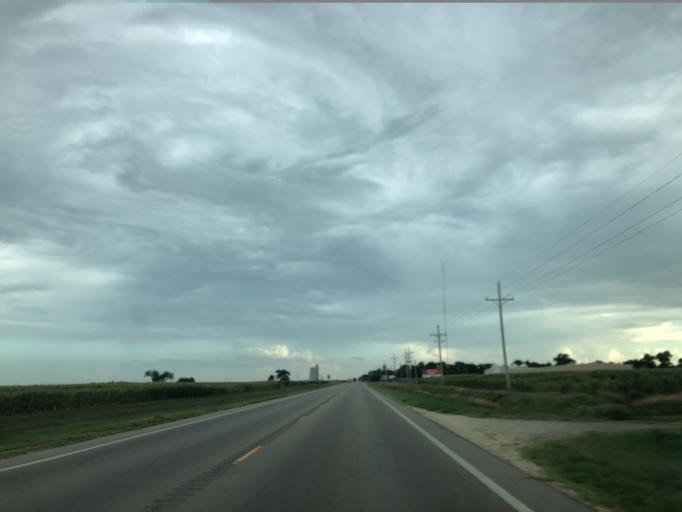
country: US
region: Kansas
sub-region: Rice County
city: Lyons
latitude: 38.2807
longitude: -98.2020
